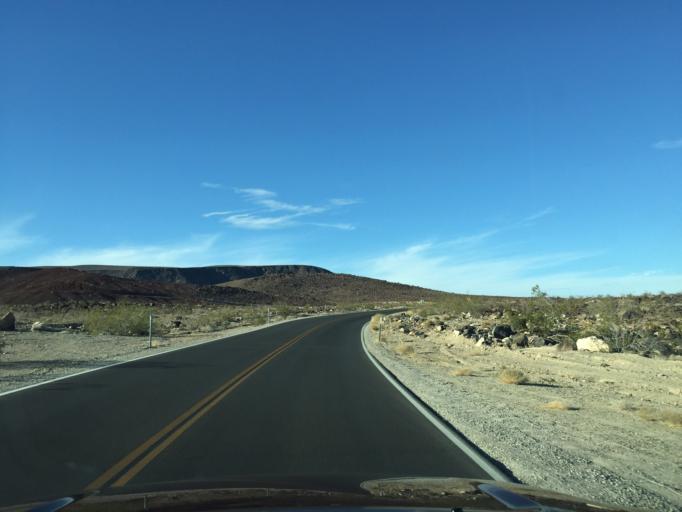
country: US
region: California
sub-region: Inyo County
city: Lone Pine
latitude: 36.3543
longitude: -117.5291
